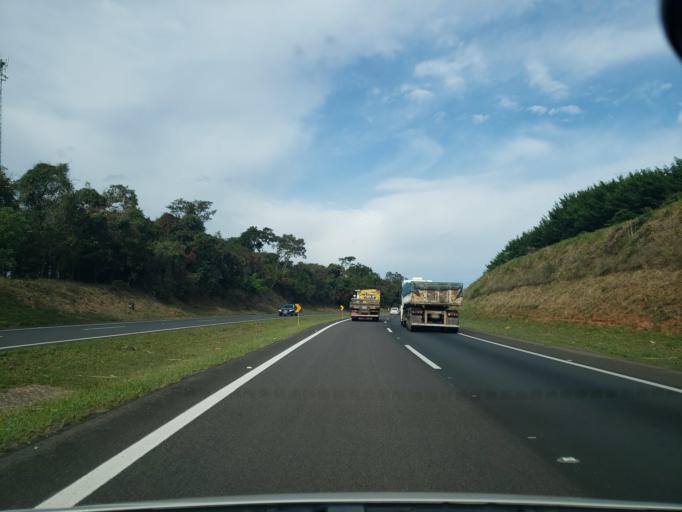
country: BR
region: Sao Paulo
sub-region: Brotas
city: Brotas
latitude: -22.2819
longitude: -47.9891
